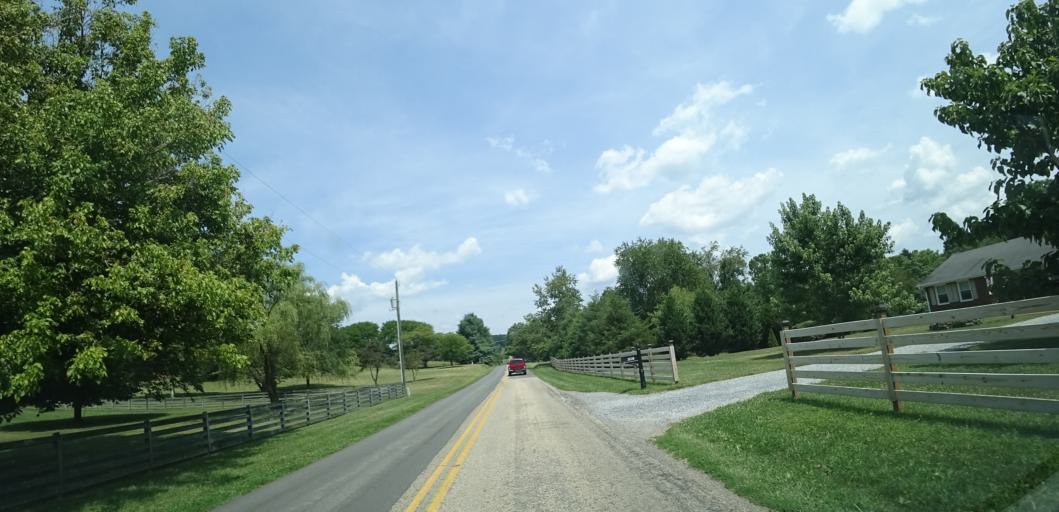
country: US
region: Virginia
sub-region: Botetourt County
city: Fincastle
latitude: 37.4669
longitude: -79.8431
